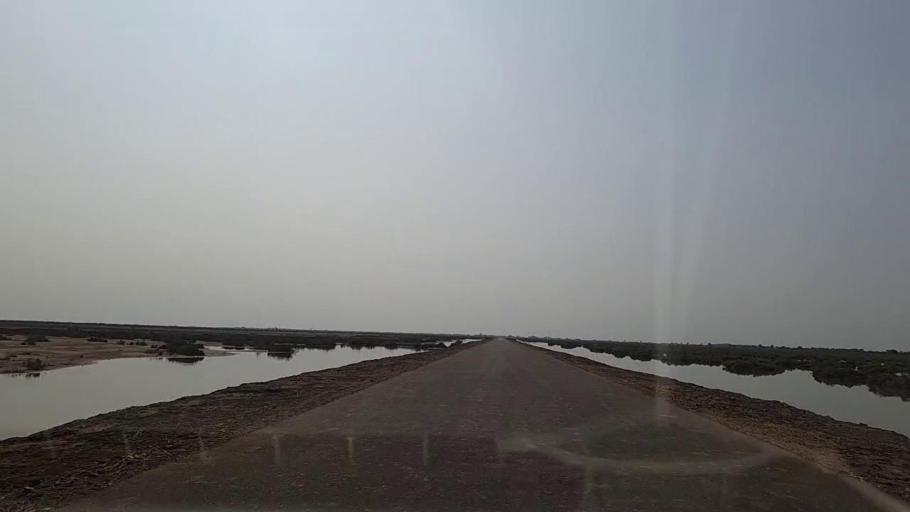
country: PK
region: Sindh
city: Chuhar Jamali
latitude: 24.2142
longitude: 67.8648
